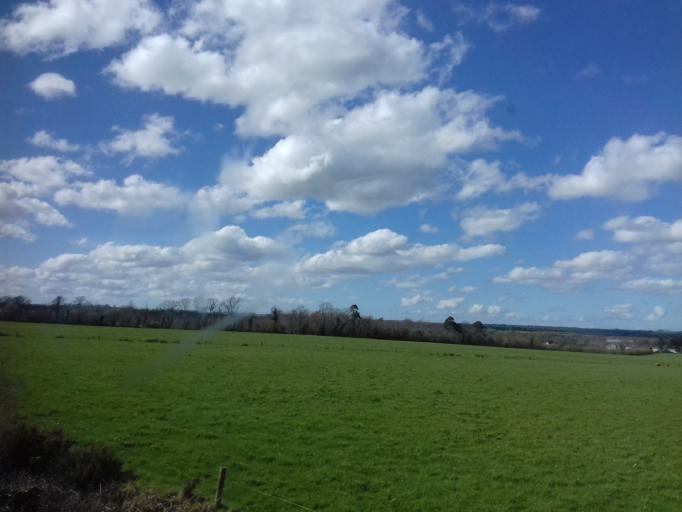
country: IE
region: Munster
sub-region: County Cork
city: Kanturk
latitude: 52.1293
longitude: -8.8350
